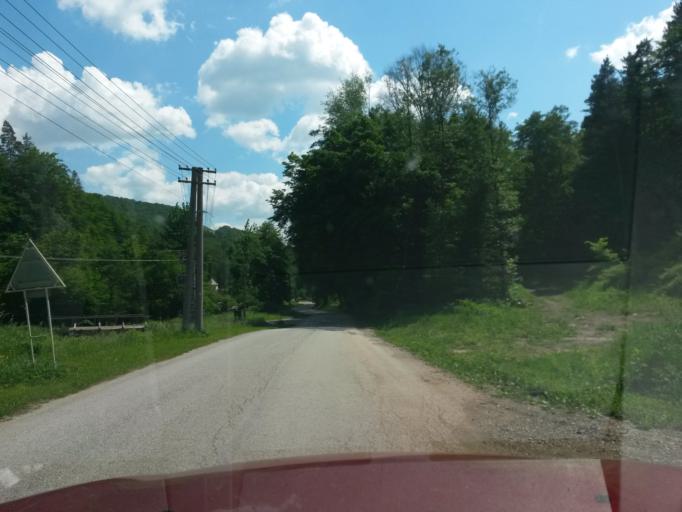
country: SK
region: Kosicky
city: Roznava
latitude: 48.6814
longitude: 20.5420
